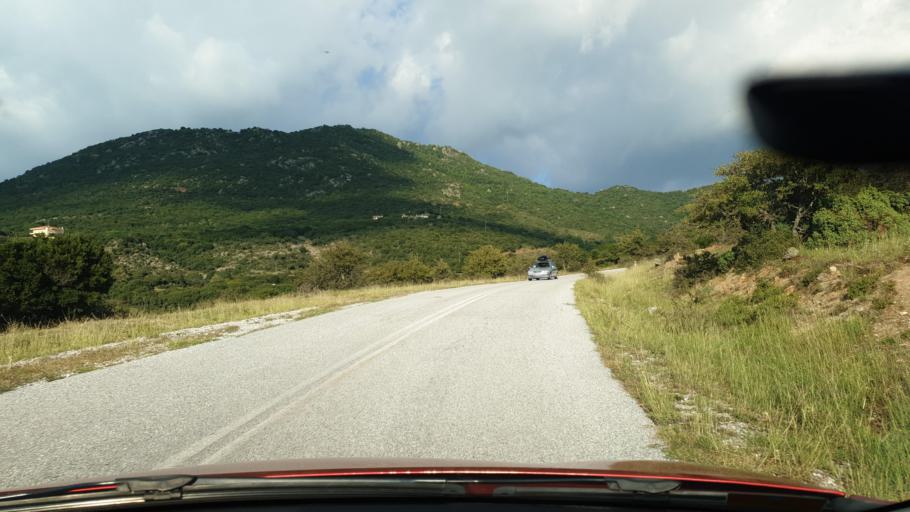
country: GR
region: Central Macedonia
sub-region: Nomos Thessalonikis
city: Peristera
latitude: 40.5258
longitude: 23.1894
